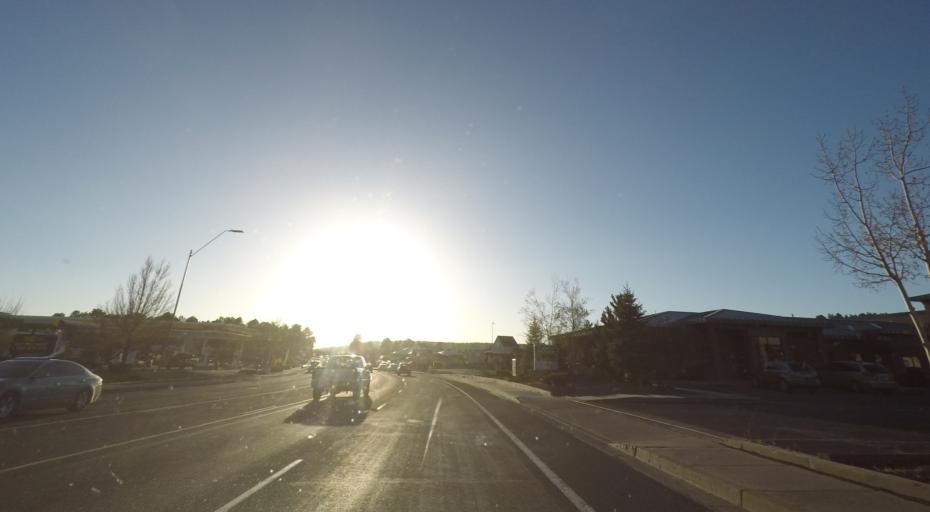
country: US
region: Arizona
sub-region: Coconino County
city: Flagstaff
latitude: 35.1916
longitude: -111.6343
